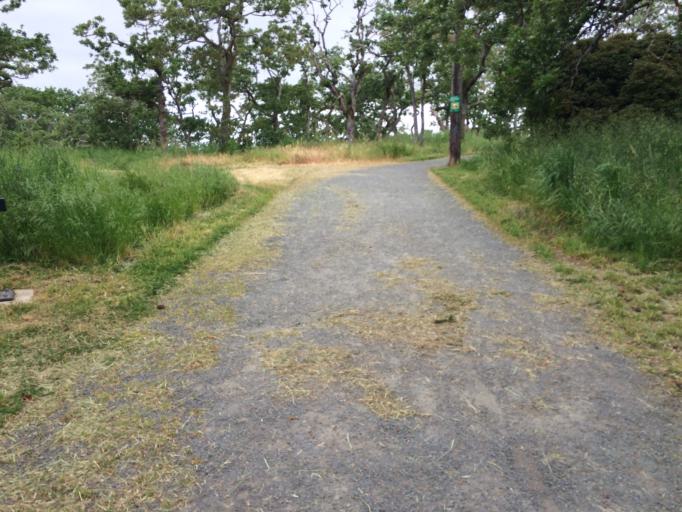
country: CA
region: British Columbia
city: Victoria
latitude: 48.4452
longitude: -123.3555
